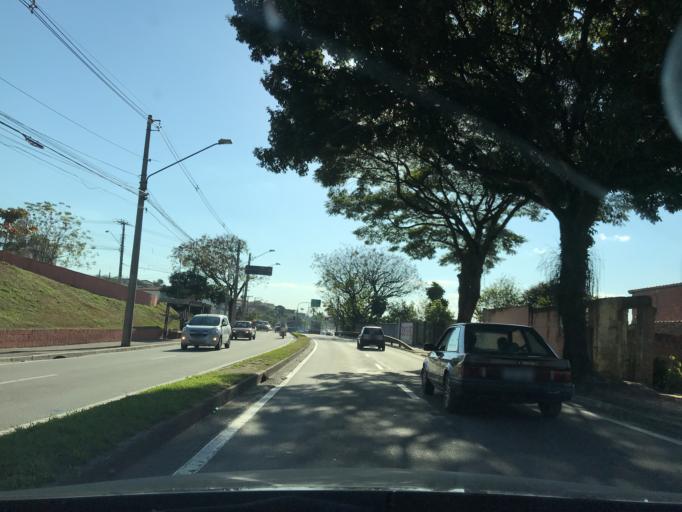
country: BR
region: Sao Paulo
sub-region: Sao Jose Dos Campos
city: Sao Jose dos Campos
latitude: -23.1777
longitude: -45.8729
